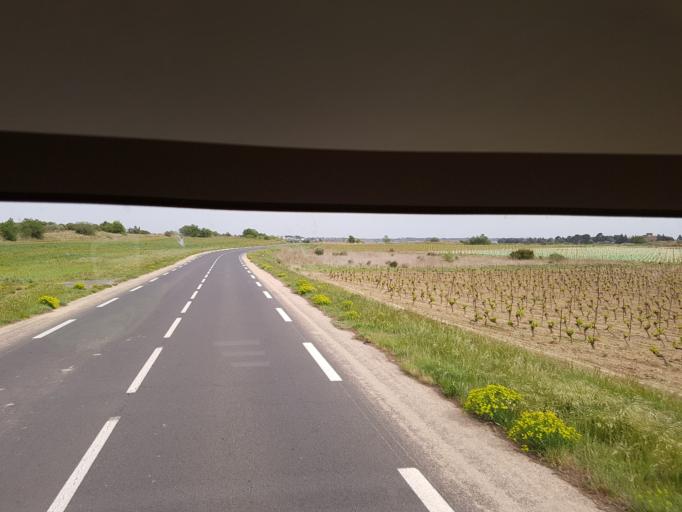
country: FR
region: Languedoc-Roussillon
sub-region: Departement de l'Herault
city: Vendres
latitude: 43.2751
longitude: 3.2020
